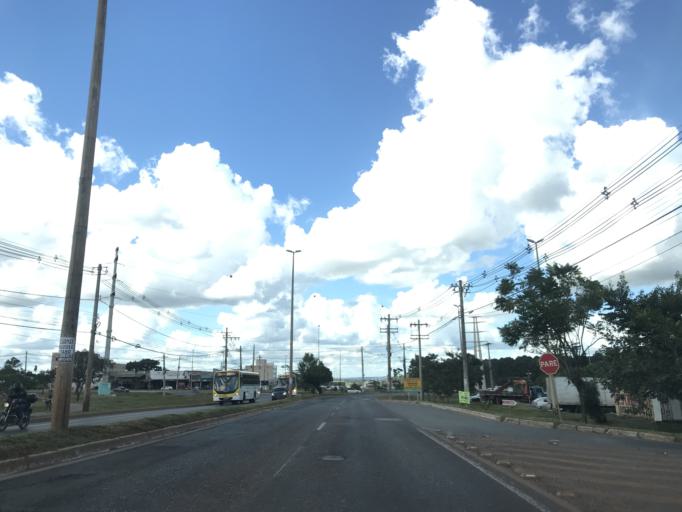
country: BR
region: Federal District
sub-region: Brasilia
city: Brasilia
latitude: -15.7590
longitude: -47.7798
